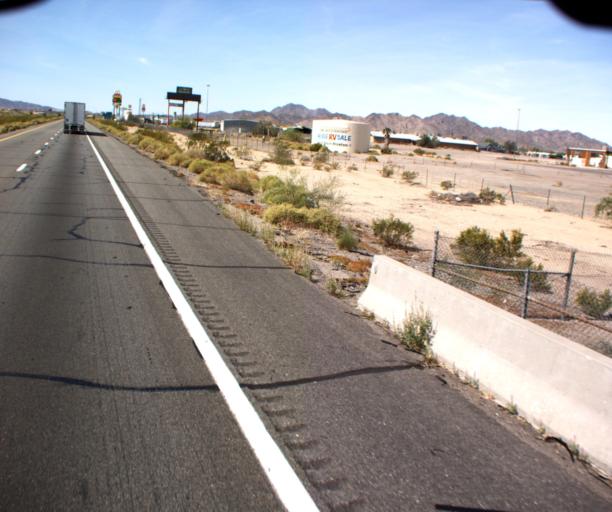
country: US
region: Arizona
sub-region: La Paz County
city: Quartzsite
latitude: 33.6613
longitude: -114.2310
